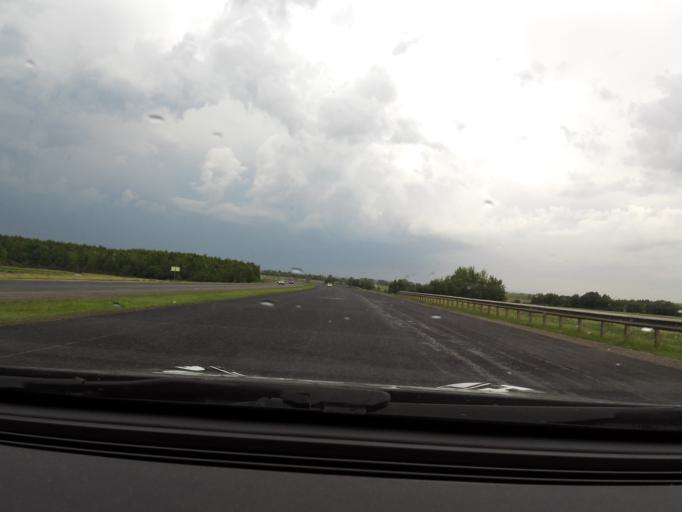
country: RU
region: Bashkortostan
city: Asanovo
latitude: 54.9616
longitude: 55.5850
